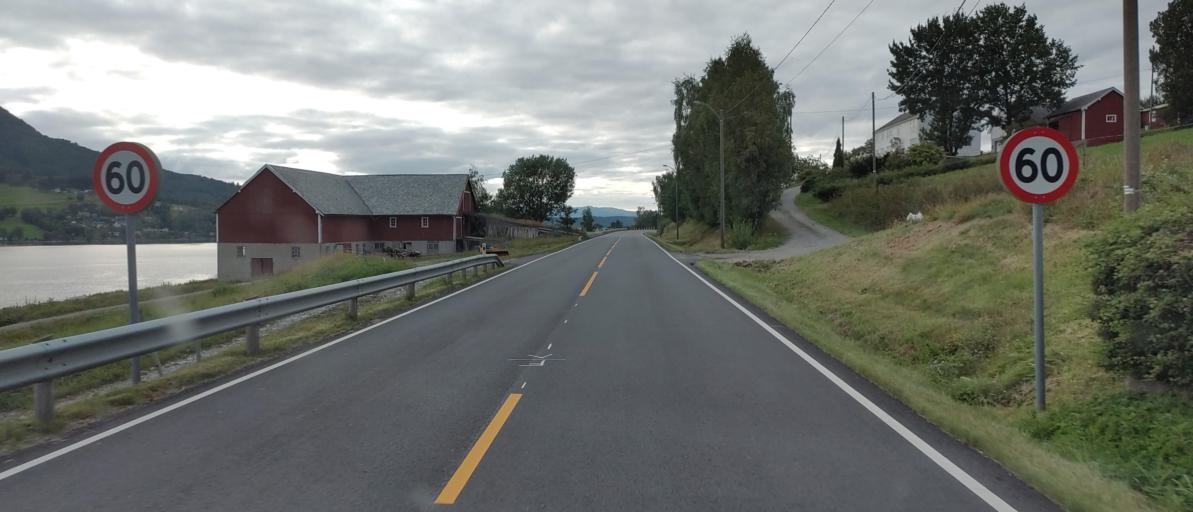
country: NO
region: More og Romsdal
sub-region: Molde
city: Hjelset
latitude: 62.6294
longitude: 7.5250
